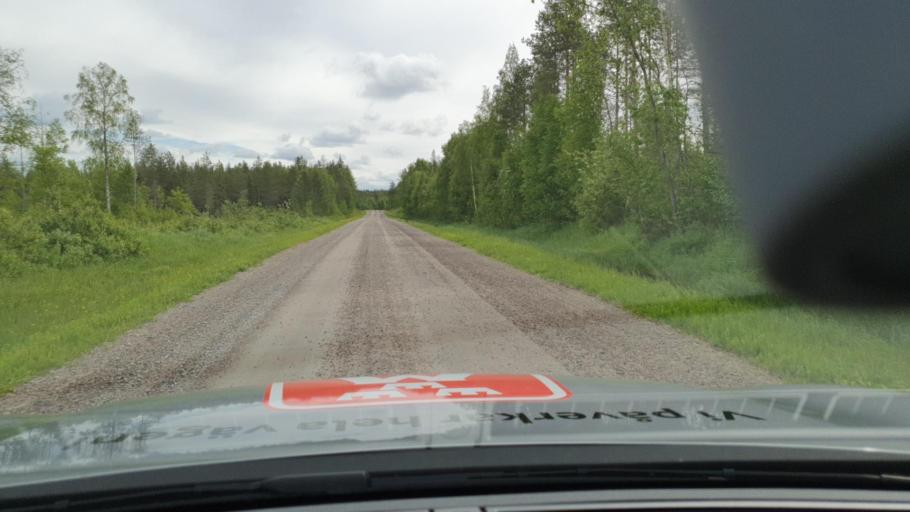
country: FI
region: Lapland
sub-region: Torniolaakso
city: Ylitornio
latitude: 65.9619
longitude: 23.6587
